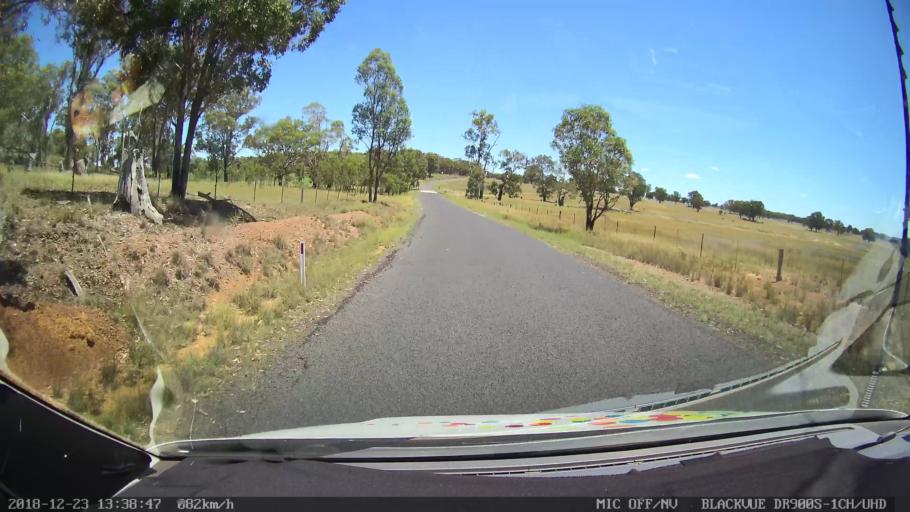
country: AU
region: New South Wales
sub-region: Armidale Dumaresq
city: Armidale
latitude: -30.4522
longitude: 151.2087
